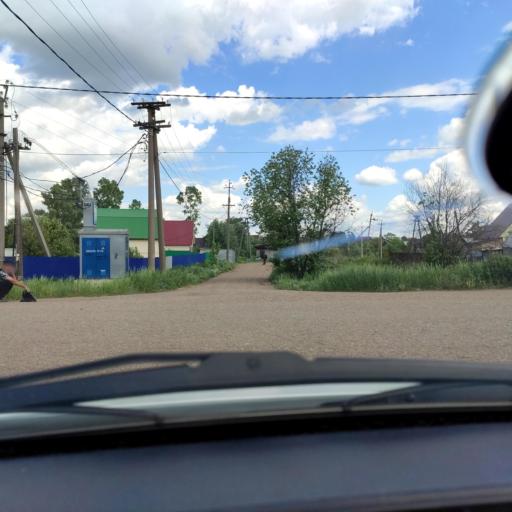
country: RU
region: Bashkortostan
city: Iglino
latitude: 54.8105
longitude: 56.3935
